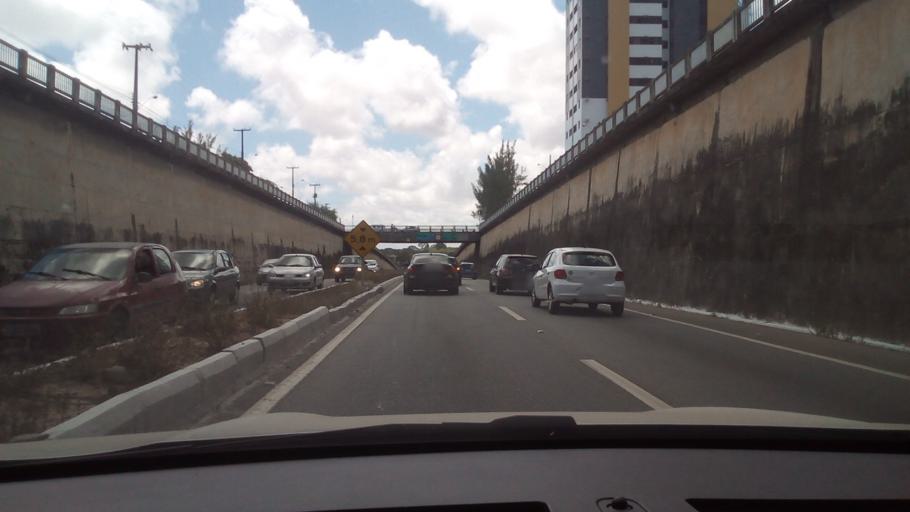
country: BR
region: Paraiba
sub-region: Joao Pessoa
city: Joao Pessoa
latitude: -7.1209
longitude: -34.8453
